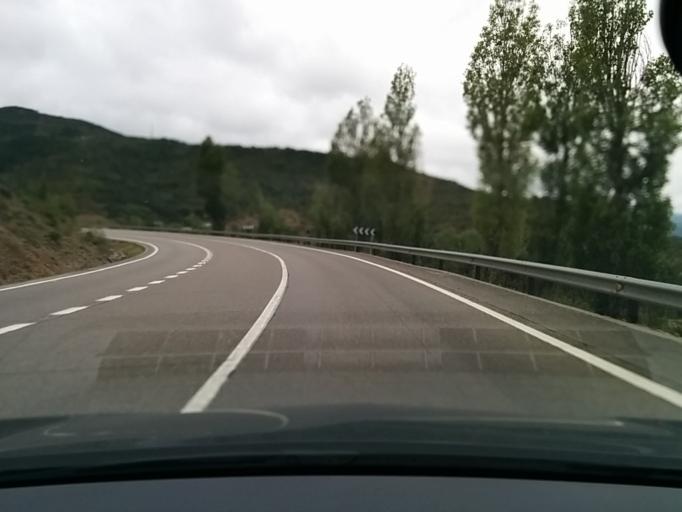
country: ES
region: Aragon
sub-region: Provincia de Huesca
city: Arguis
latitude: 42.3997
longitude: -0.3805
